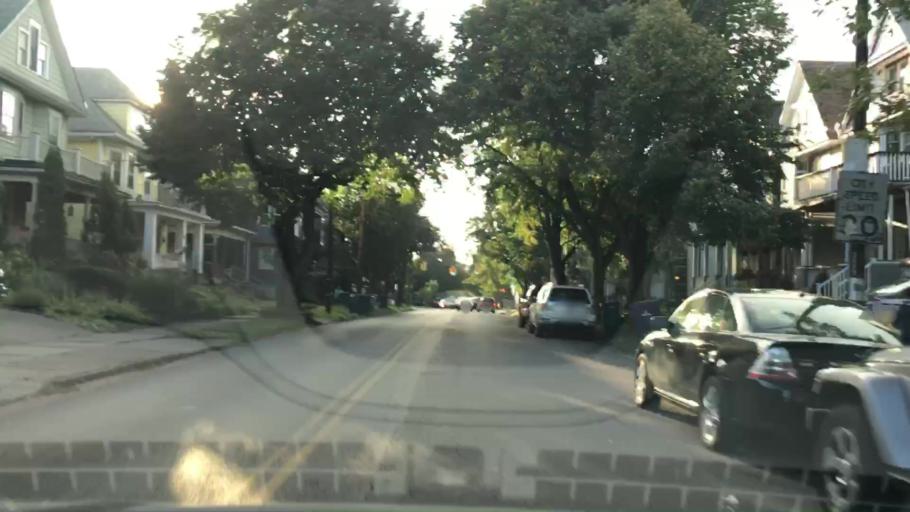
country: US
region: New York
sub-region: Erie County
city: Buffalo
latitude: 42.9113
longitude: -78.8807
